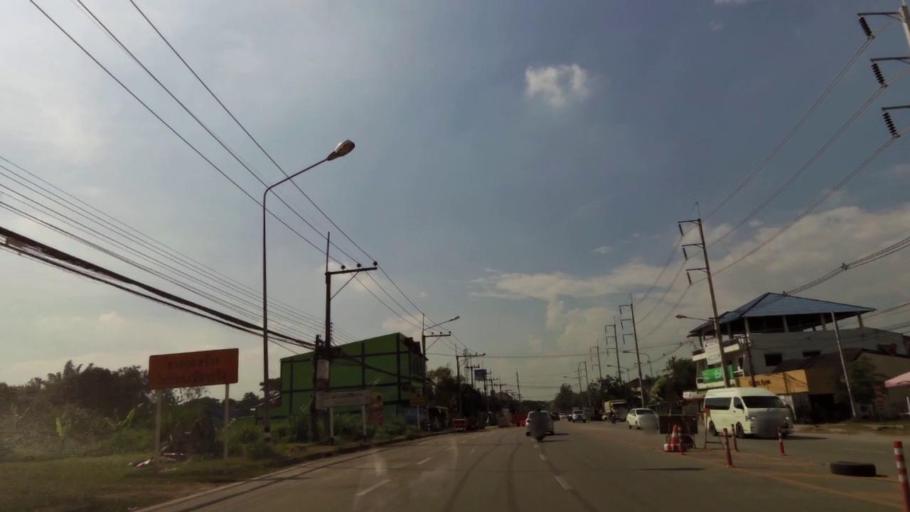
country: TH
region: Chiang Rai
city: Chiang Rai
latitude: 19.8801
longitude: 99.7942
